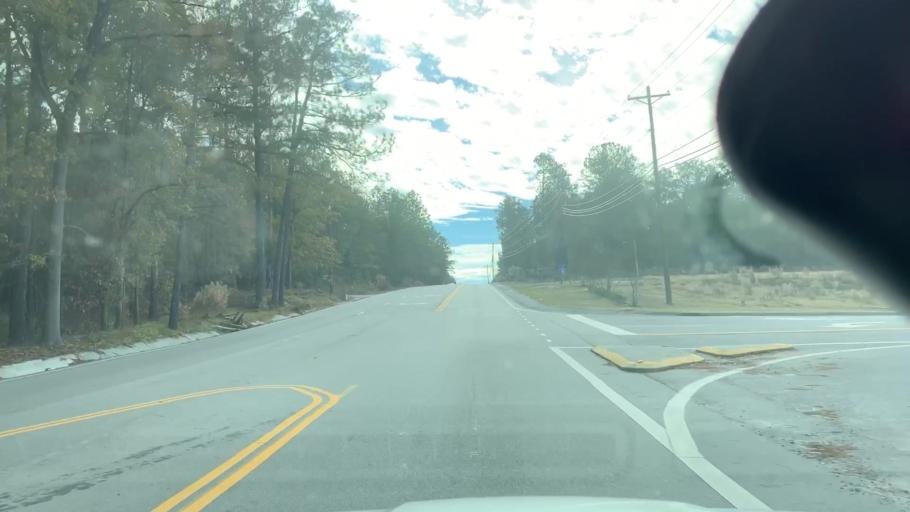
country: US
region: South Carolina
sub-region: Richland County
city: Woodfield
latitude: 34.0760
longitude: -80.9188
